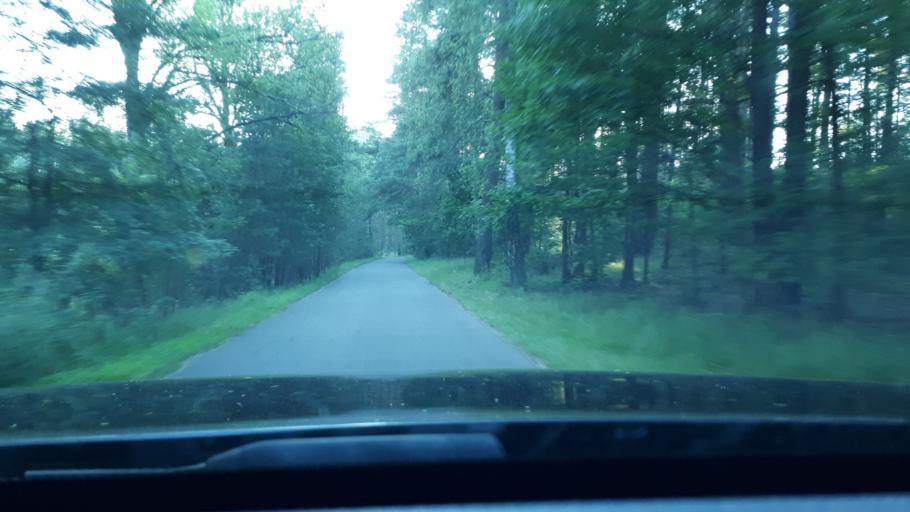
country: PL
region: Warmian-Masurian Voivodeship
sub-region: Powiat olsztynski
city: Stawiguda
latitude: 53.5879
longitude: 20.4589
